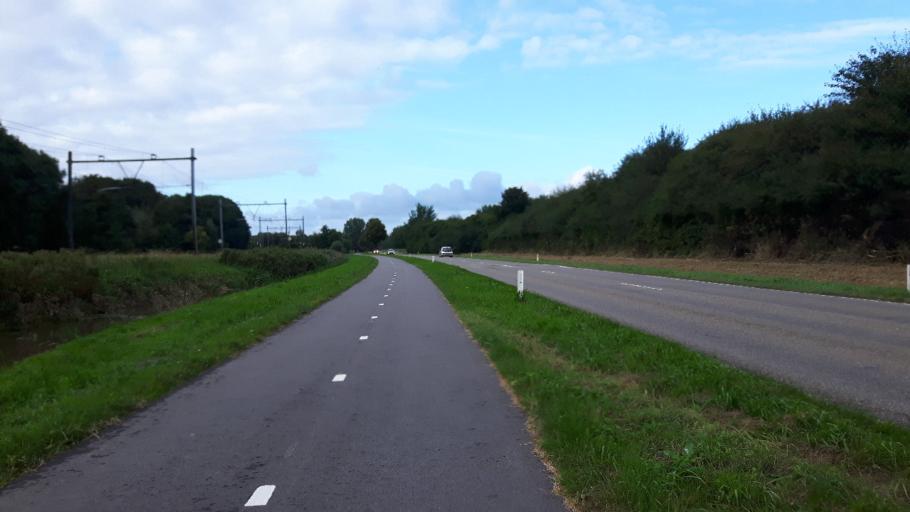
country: NL
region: North Holland
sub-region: Gemeente Hoorn
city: Hoorn
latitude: 52.6402
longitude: 5.0226
